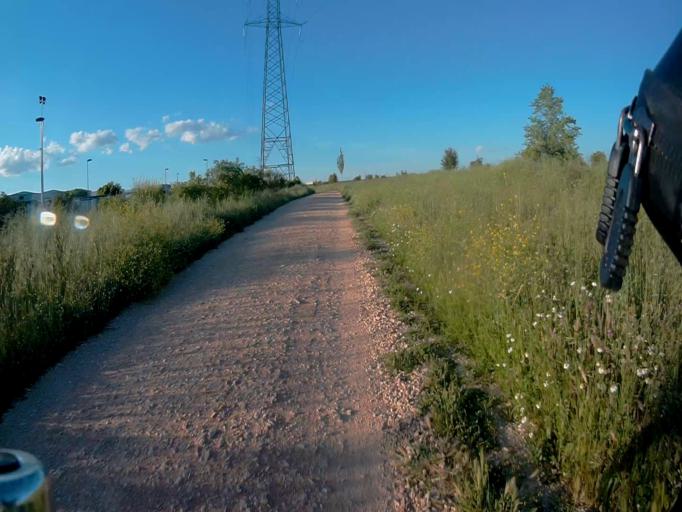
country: ES
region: Madrid
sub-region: Provincia de Madrid
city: Fuenlabrada
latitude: 40.3049
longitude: -3.7987
